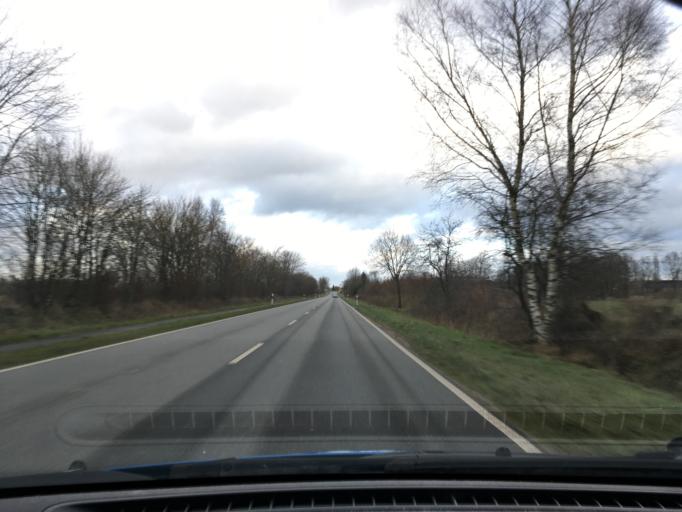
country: DE
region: Schleswig-Holstein
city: Kaisborstel
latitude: 54.0253
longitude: 9.4759
